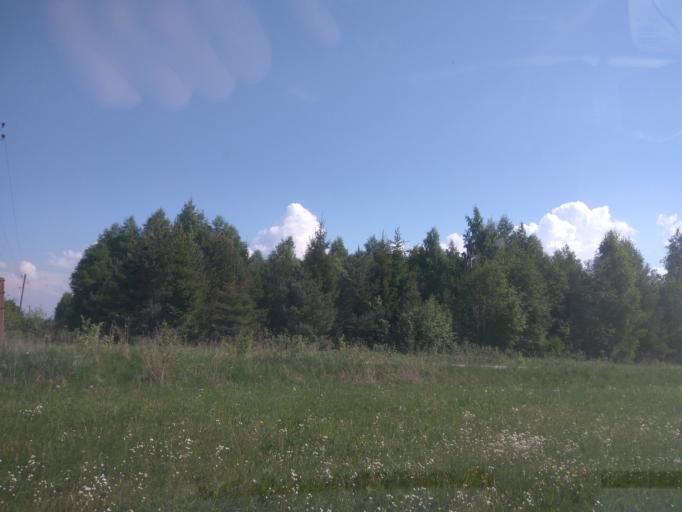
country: LV
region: Kuldigas Rajons
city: Kuldiga
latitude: 57.1755
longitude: 22.0146
